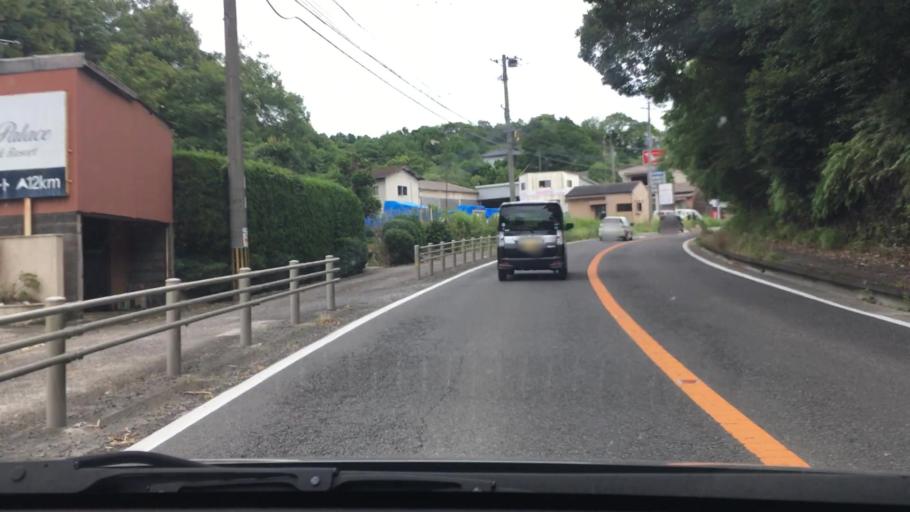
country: JP
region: Nagasaki
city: Togitsu
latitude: 32.9823
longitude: 129.7812
